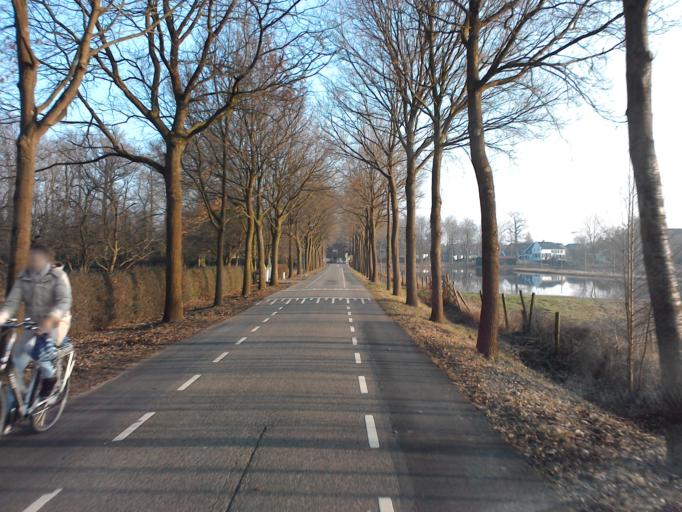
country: NL
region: Utrecht
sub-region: Gemeente Bunnik
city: Bunnik
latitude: 52.0708
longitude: 5.2018
